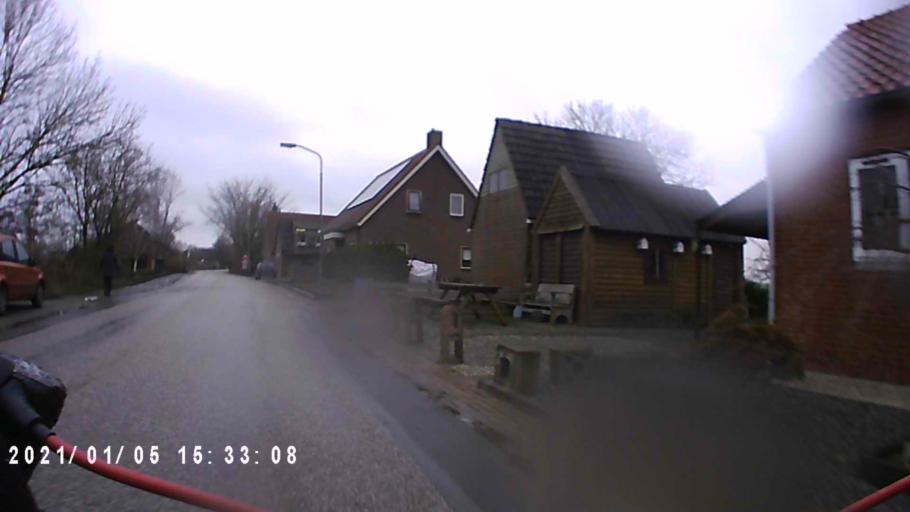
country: DE
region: Lower Saxony
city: Bunde
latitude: 53.2079
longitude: 7.1791
